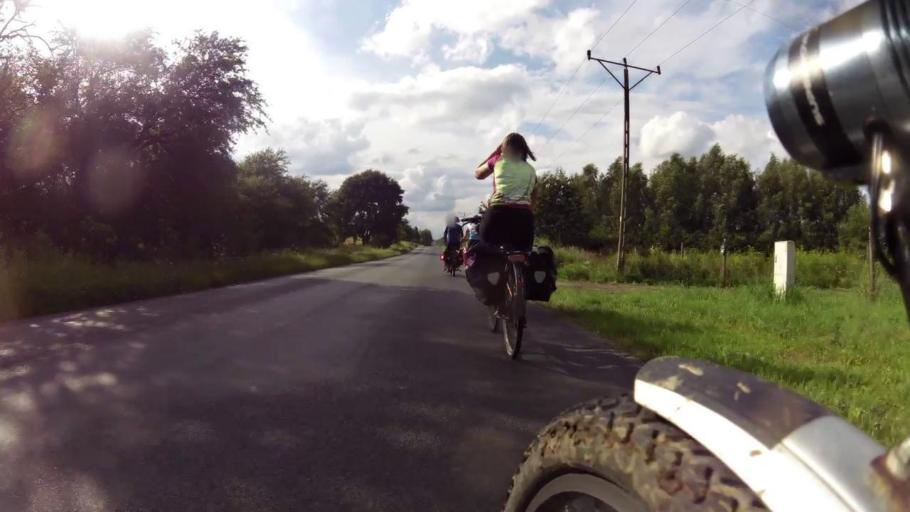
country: PL
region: West Pomeranian Voivodeship
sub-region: Powiat gryfinski
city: Gryfino
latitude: 53.2372
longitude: 14.5139
